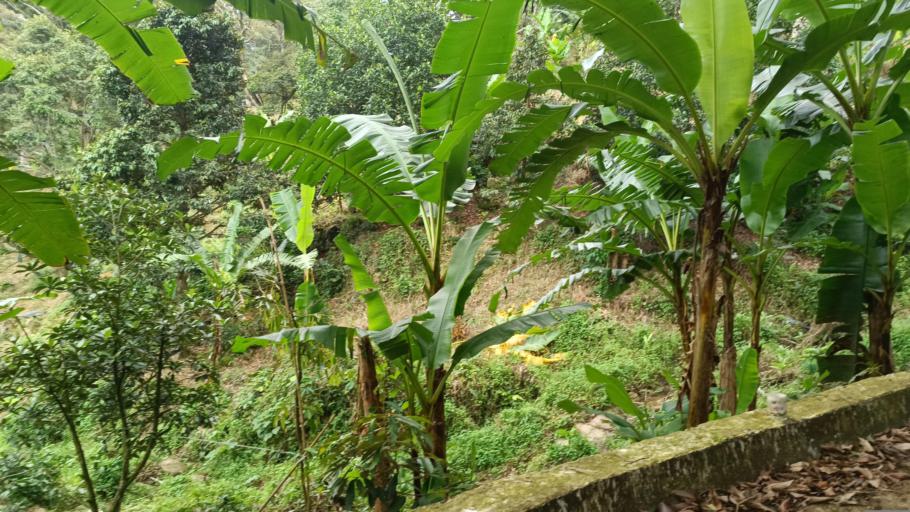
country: MY
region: Penang
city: Nibong Tebal
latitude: 5.2325
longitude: 100.5093
